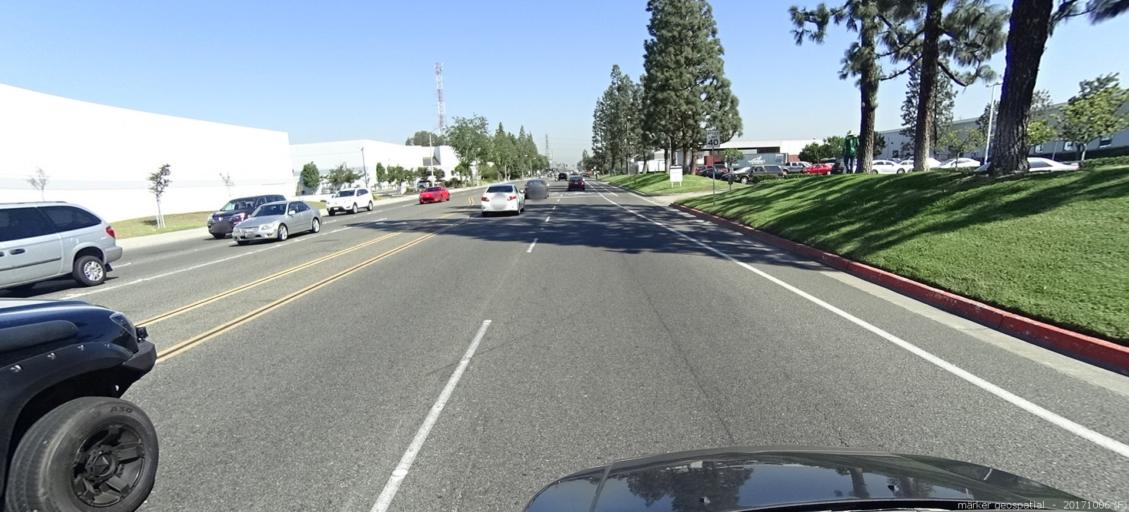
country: US
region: California
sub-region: Orange County
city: Stanton
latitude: 33.7882
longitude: -118.0057
